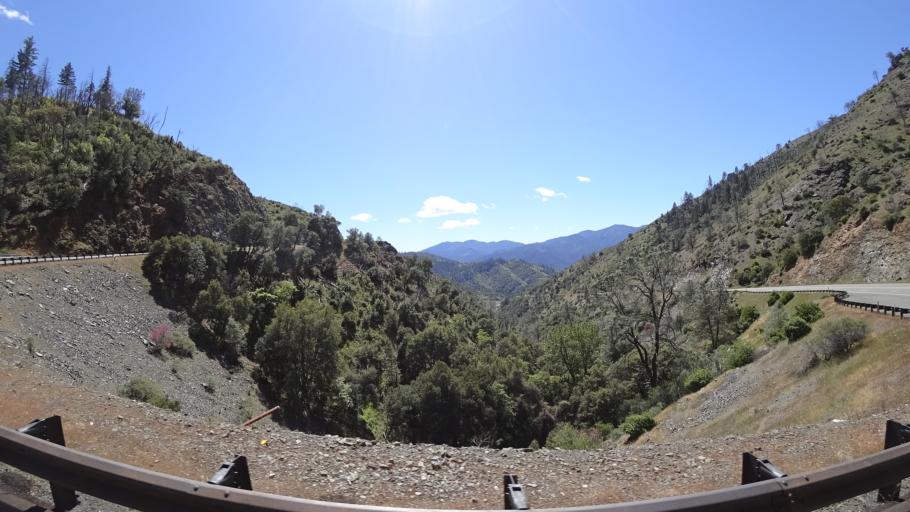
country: US
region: California
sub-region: Trinity County
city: Weaverville
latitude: 40.7422
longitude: -122.9983
